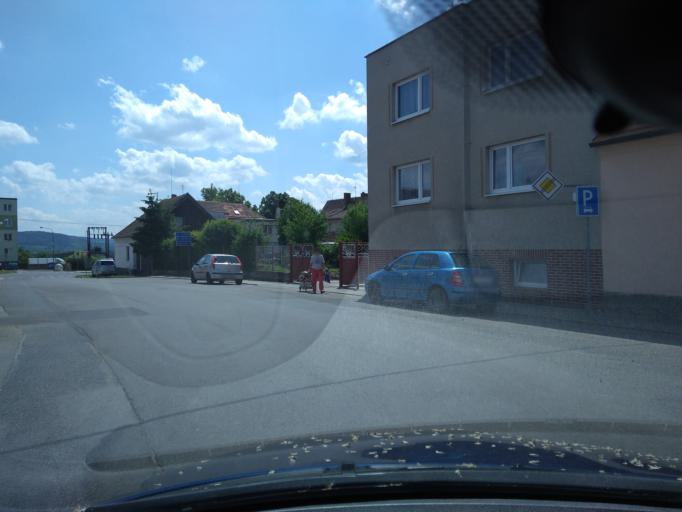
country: CZ
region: Plzensky
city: Prestice
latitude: 49.5691
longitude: 13.3255
